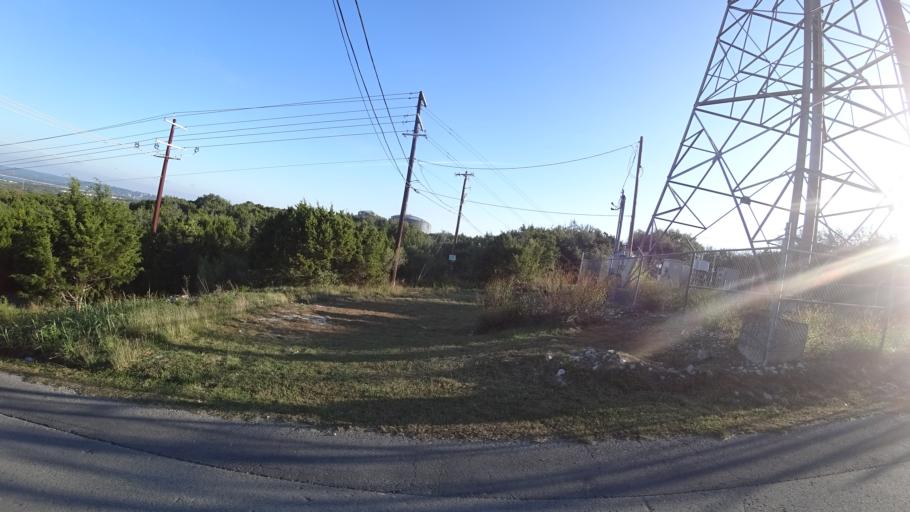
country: US
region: Texas
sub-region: Travis County
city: Hudson Bend
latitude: 30.3697
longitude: -97.8871
